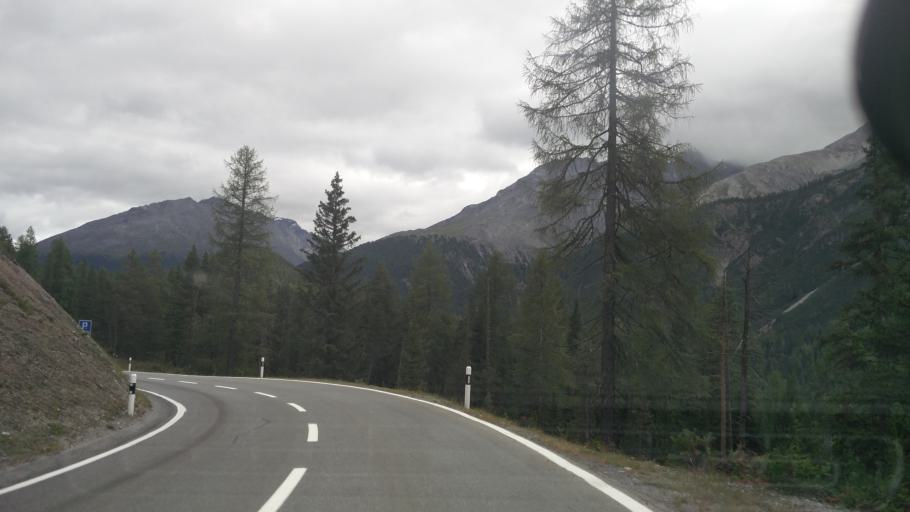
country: CH
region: Grisons
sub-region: Inn District
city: Zernez
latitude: 46.6622
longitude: 10.1713
